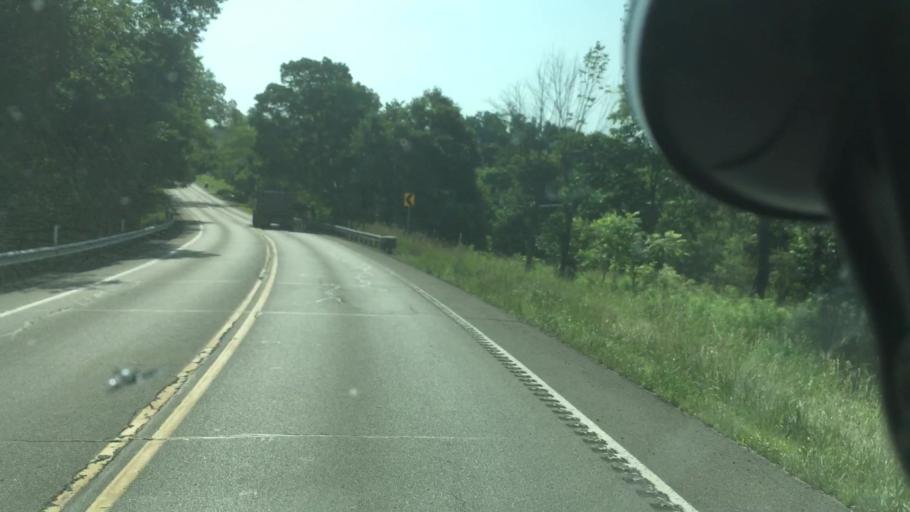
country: US
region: Pennsylvania
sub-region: Lawrence County
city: New Castle
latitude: 41.0130
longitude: -80.2423
